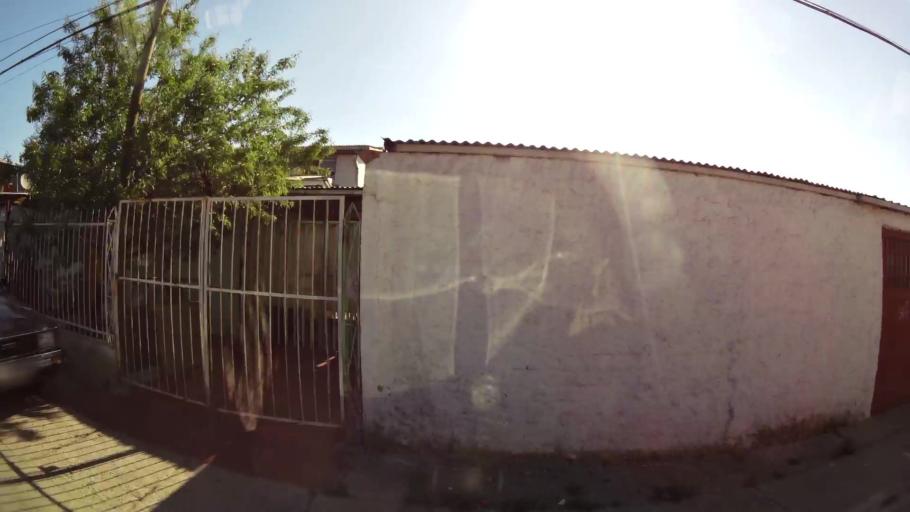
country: CL
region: Santiago Metropolitan
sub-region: Provincia de Santiago
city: La Pintana
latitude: -33.5764
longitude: -70.6480
